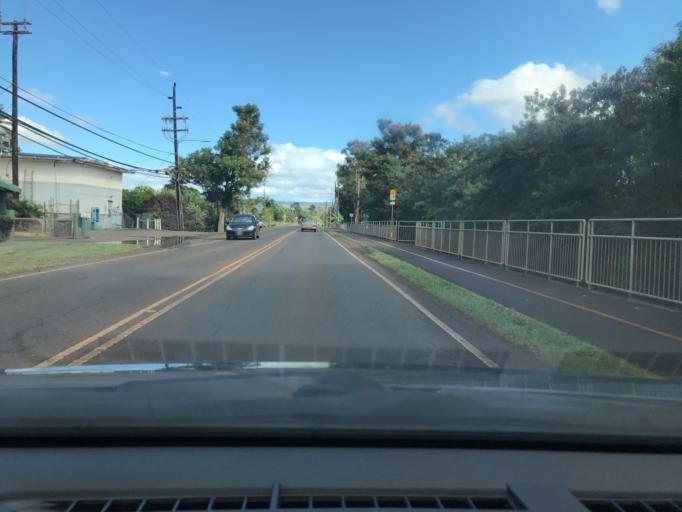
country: US
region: Hawaii
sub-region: Honolulu County
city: Waialua
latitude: 21.5757
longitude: -158.1178
